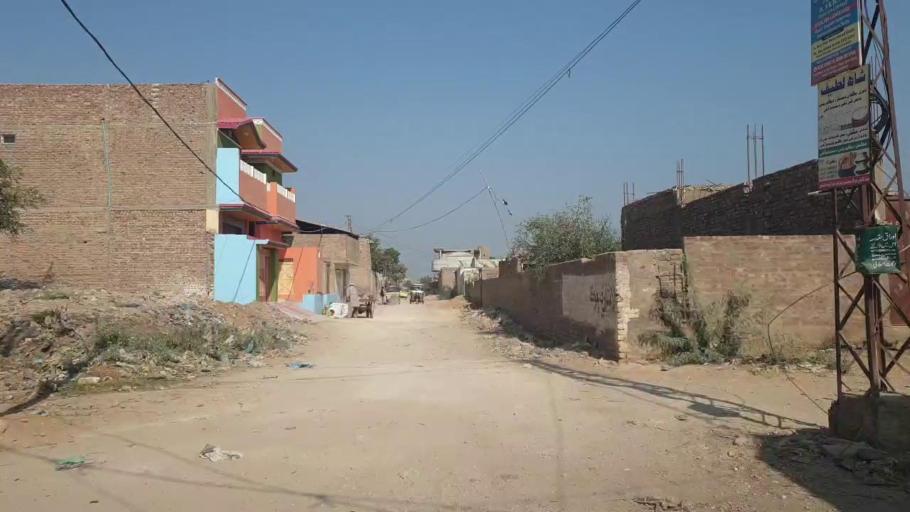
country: PK
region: Sindh
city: Jamshoro
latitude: 25.4084
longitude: 68.2798
